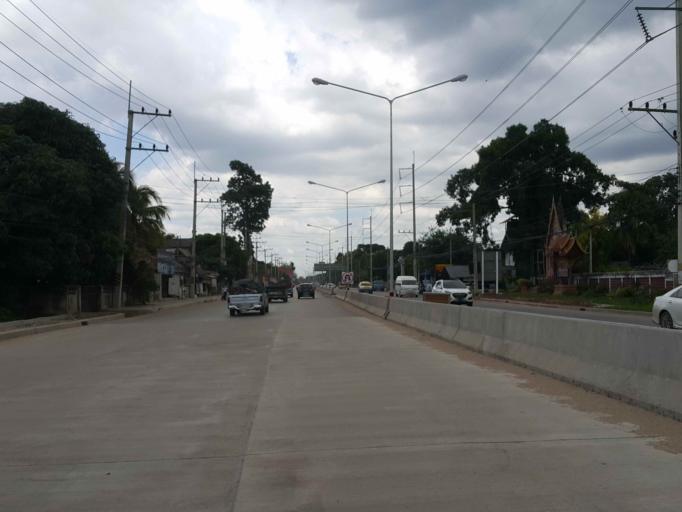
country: TH
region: Chiang Mai
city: Chiang Mai
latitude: 18.8628
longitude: 98.9657
